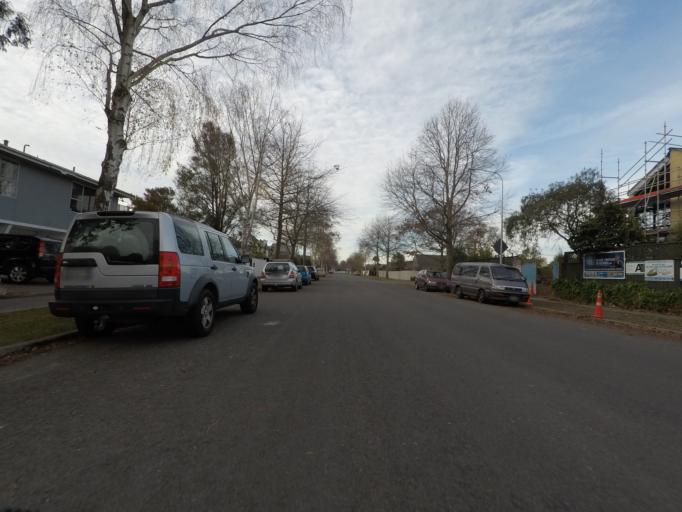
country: NZ
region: Canterbury
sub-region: Christchurch City
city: Christchurch
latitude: -43.5160
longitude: 172.6166
